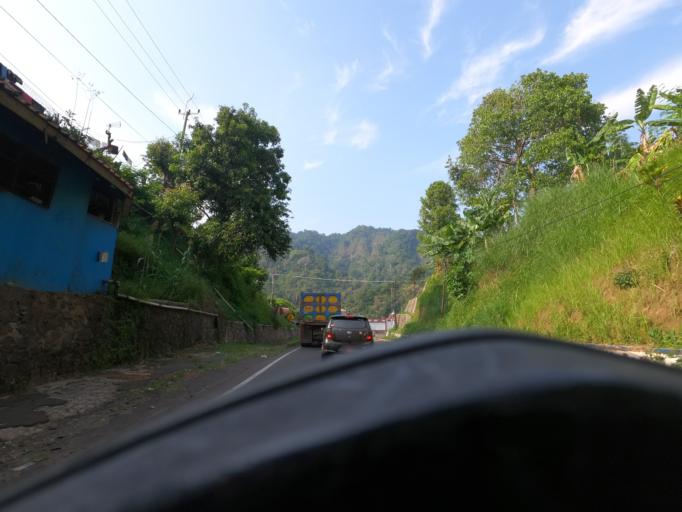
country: ID
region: West Java
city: Lembang
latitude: -6.6287
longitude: 107.7213
